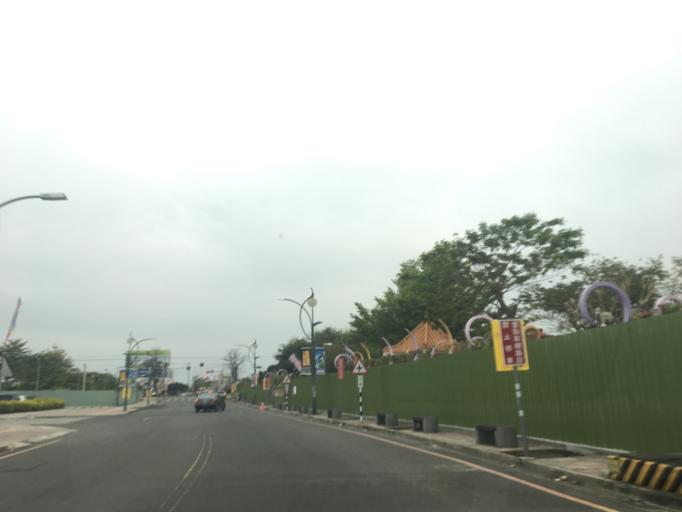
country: TW
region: Taiwan
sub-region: Nantou
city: Nantou
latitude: 23.8968
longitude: 120.5321
